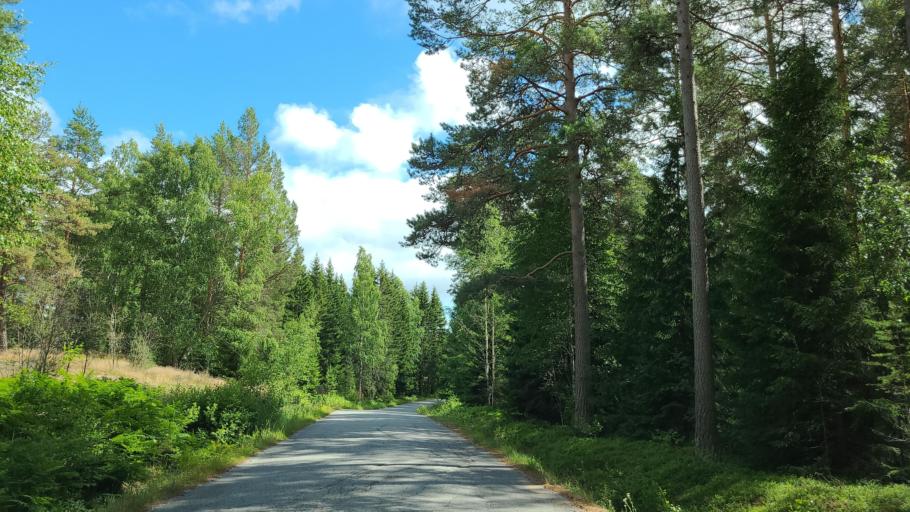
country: FI
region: Varsinais-Suomi
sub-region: Aboland-Turunmaa
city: Nagu
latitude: 60.1736
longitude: 22.0416
